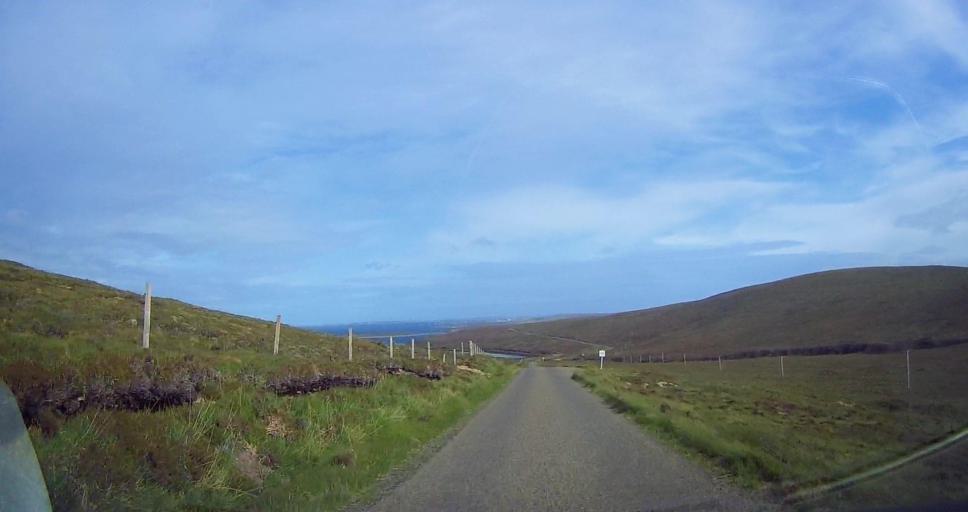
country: GB
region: Scotland
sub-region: Orkney Islands
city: Stromness
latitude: 58.8747
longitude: -3.2444
